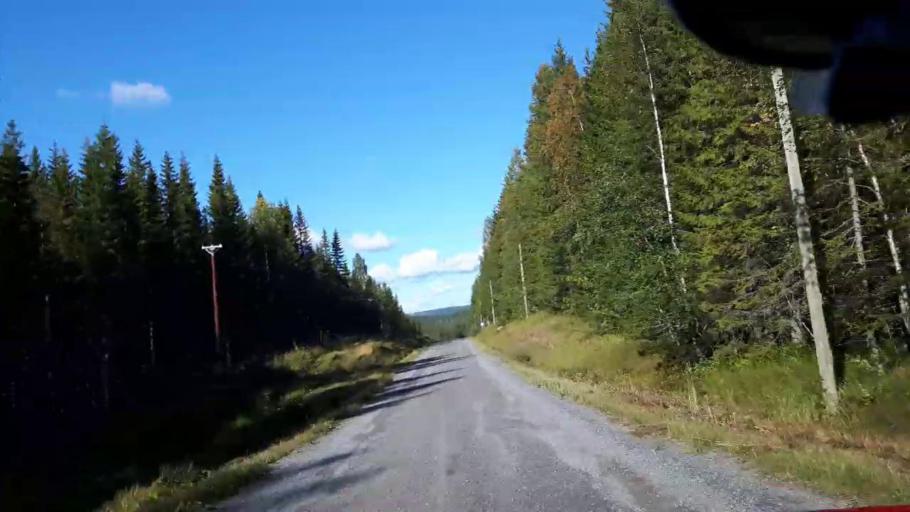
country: SE
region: Jaemtland
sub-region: Ragunda Kommun
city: Hammarstrand
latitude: 63.5094
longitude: 16.0450
